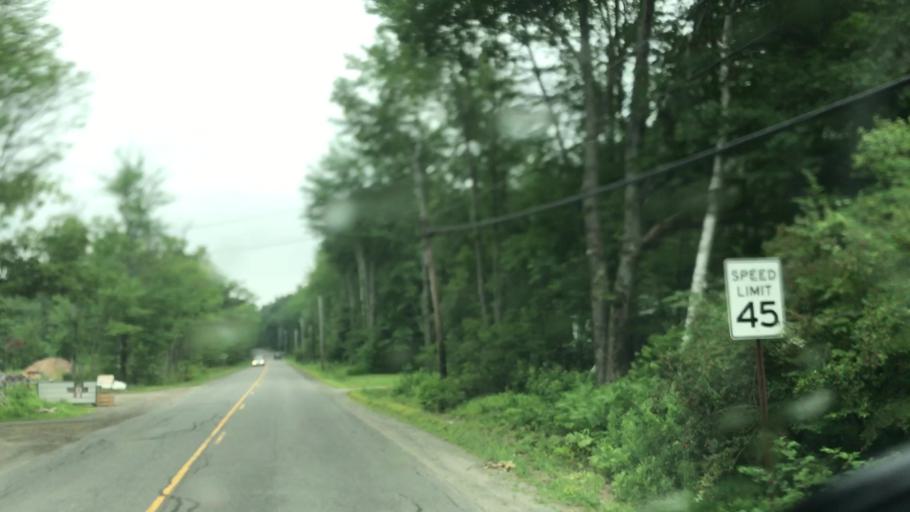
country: US
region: Maine
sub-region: Penobscot County
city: Orono
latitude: 44.8901
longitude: -68.7043
